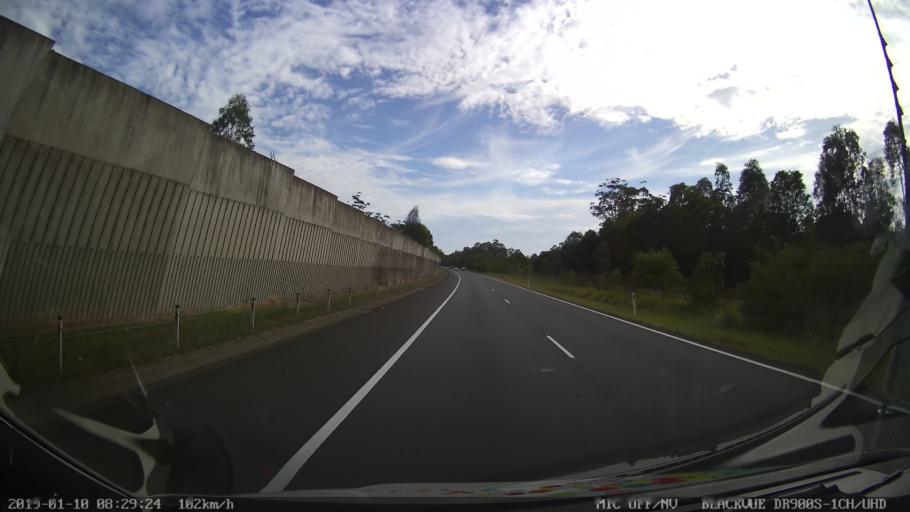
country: AU
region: New South Wales
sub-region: Coffs Harbour
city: Bonville
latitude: -30.3836
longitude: 153.0455
